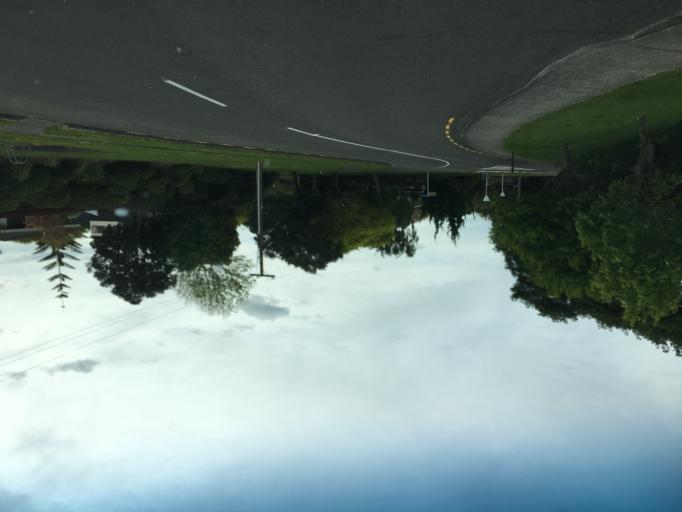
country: NZ
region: Manawatu-Wanganui
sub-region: Palmerston North City
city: Palmerston North
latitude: -40.3772
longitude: 175.5791
